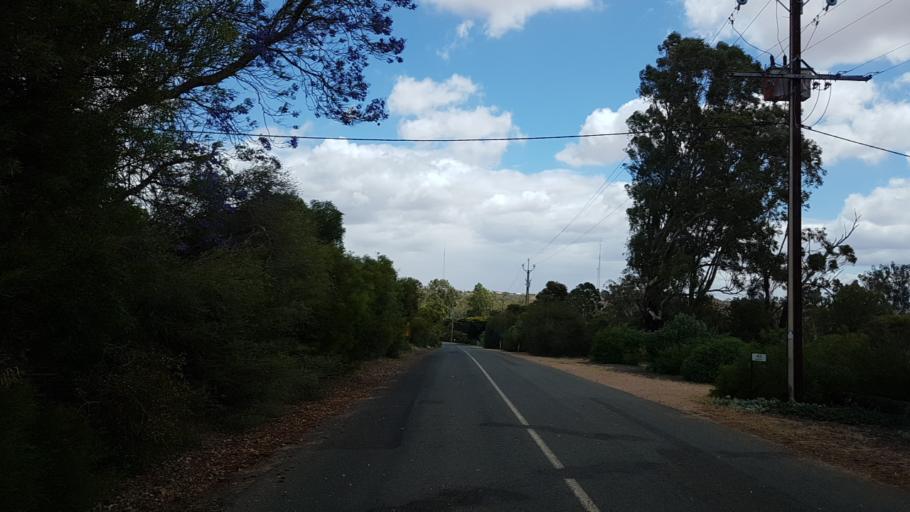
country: AU
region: South Australia
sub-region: Loxton Waikerie
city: Waikerie
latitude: -34.1661
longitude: 140.0355
